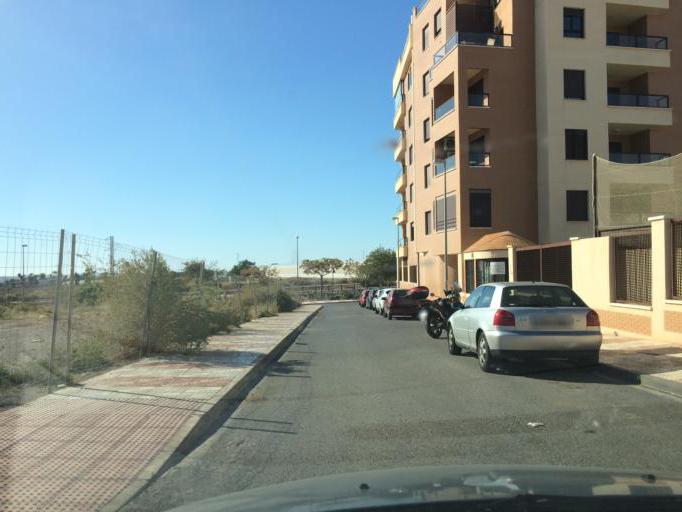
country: ES
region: Andalusia
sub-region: Provincia de Almeria
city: Aguadulce
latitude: 36.8023
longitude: -2.5858
